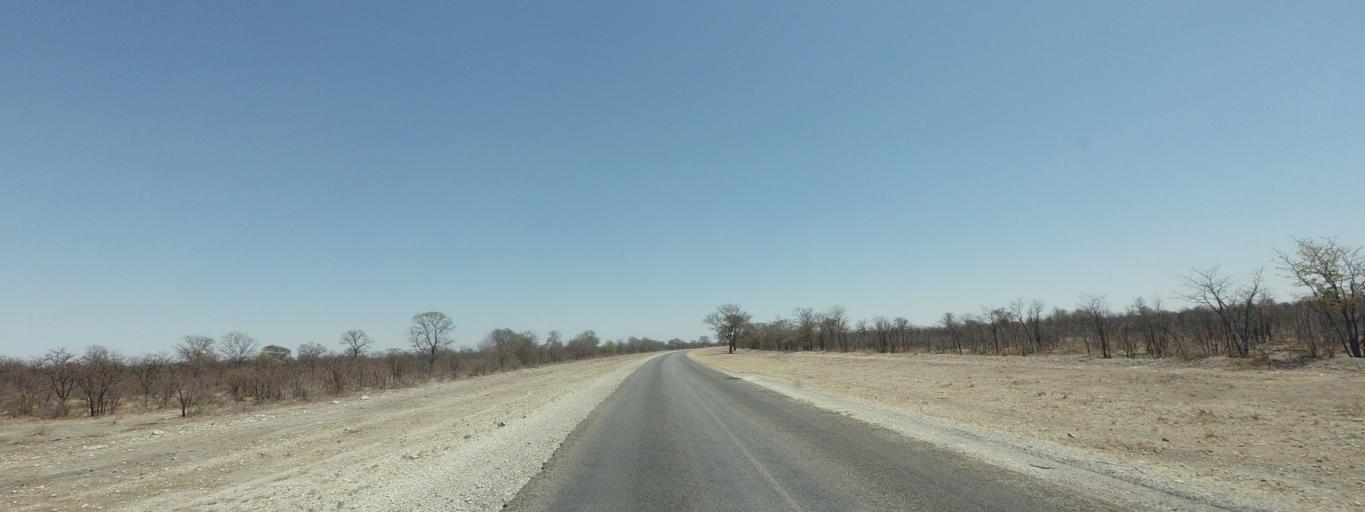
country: BW
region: Central
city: Nata
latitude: -20.3750
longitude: 26.3234
